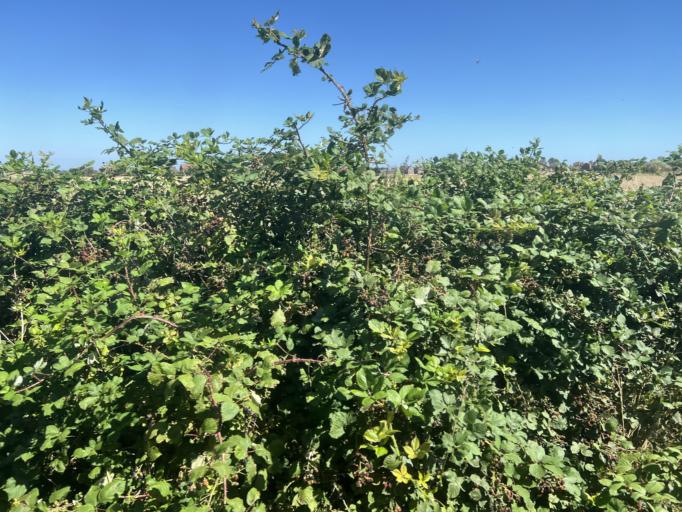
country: GB
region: England
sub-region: Lincolnshire
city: Wainfleet All Saints
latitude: 53.1081
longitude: 0.2284
